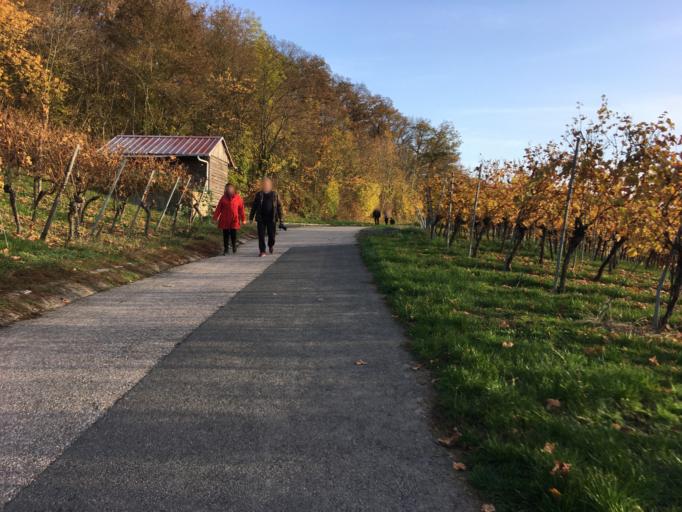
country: DE
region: Baden-Wuerttemberg
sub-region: Regierungsbezirk Stuttgart
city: Erlenbach
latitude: 49.1478
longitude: 9.2543
